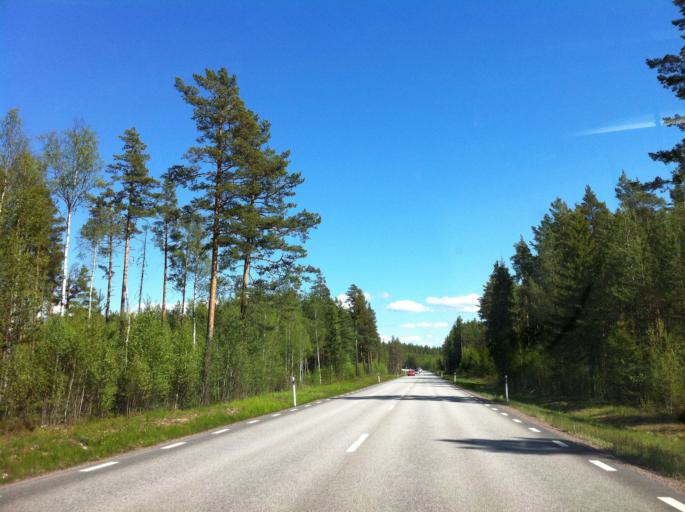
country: SE
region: Dalarna
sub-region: Rattviks Kommun
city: Vikarbyn
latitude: 60.9143
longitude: 14.8899
